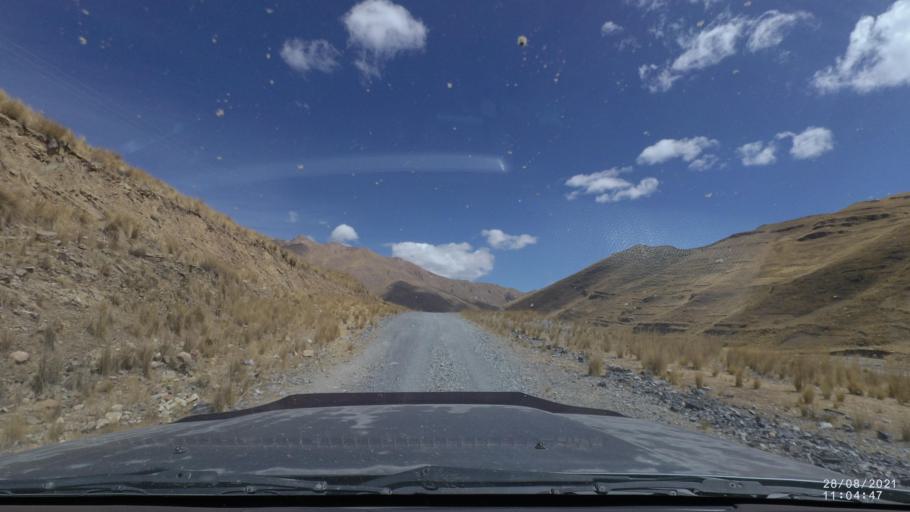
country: BO
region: Cochabamba
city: Cochabamba
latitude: -17.1732
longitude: -66.2843
